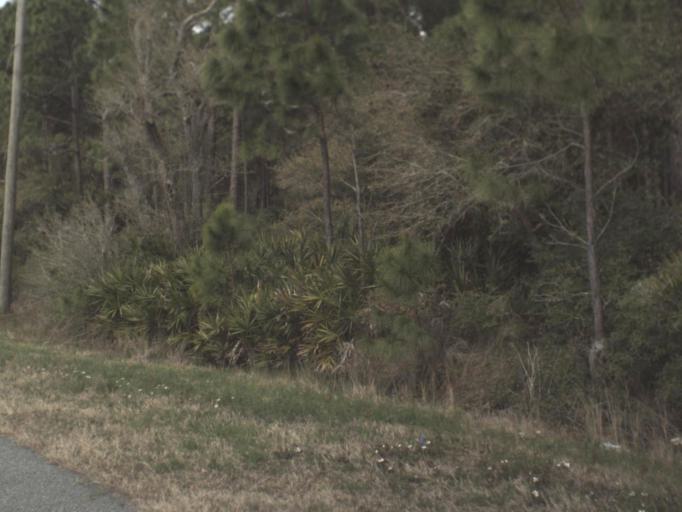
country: US
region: Florida
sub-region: Franklin County
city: Eastpoint
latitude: 29.7588
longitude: -84.8238
